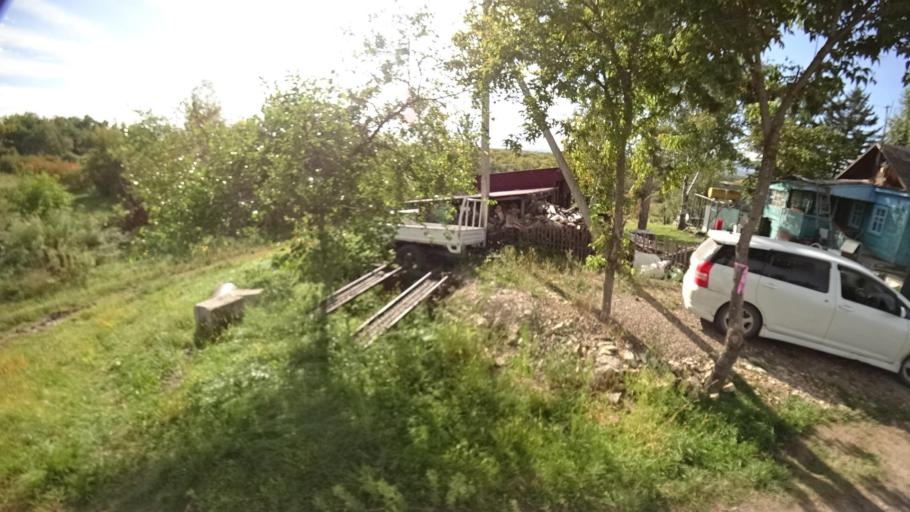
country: RU
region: Primorskiy
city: Dostoyevka
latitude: 44.3060
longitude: 133.4482
